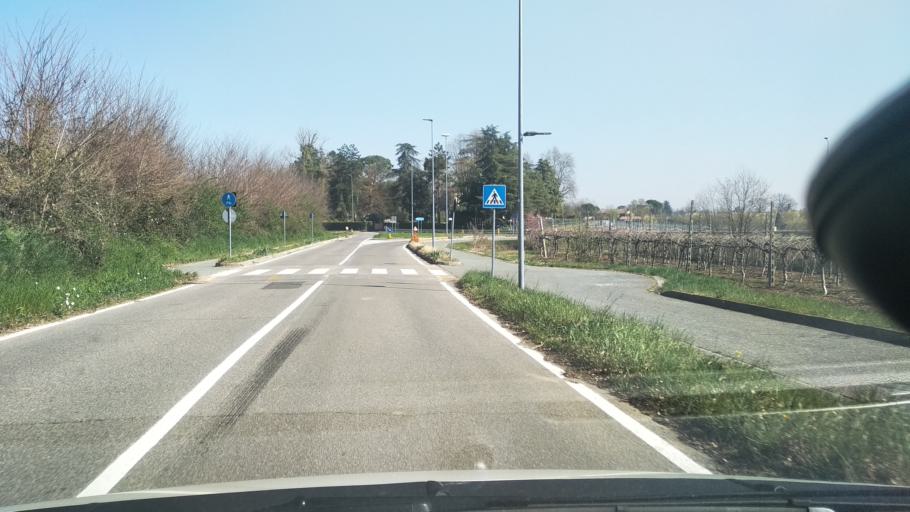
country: IT
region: Emilia-Romagna
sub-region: Provincia di Ravenna
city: Faenza
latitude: 44.2674
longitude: 11.8733
